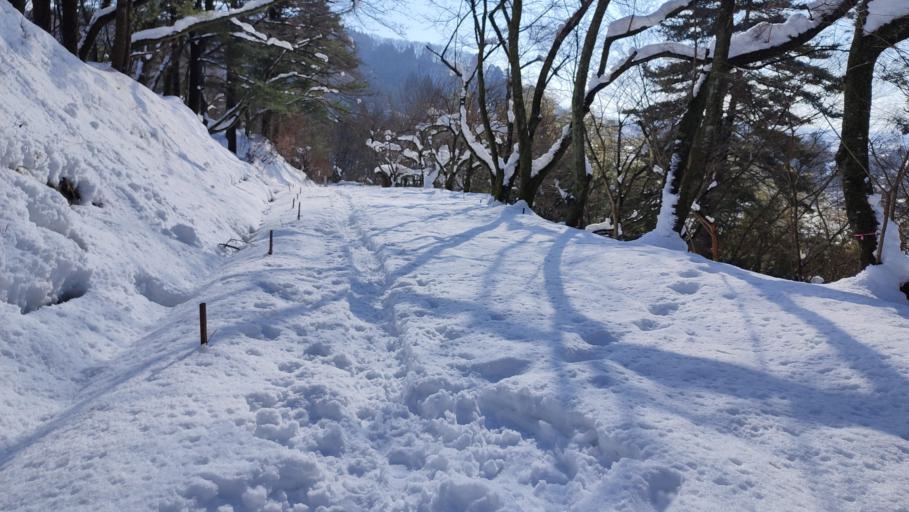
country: JP
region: Akita
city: Kakunodatemachi
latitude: 39.6047
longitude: 140.5620
